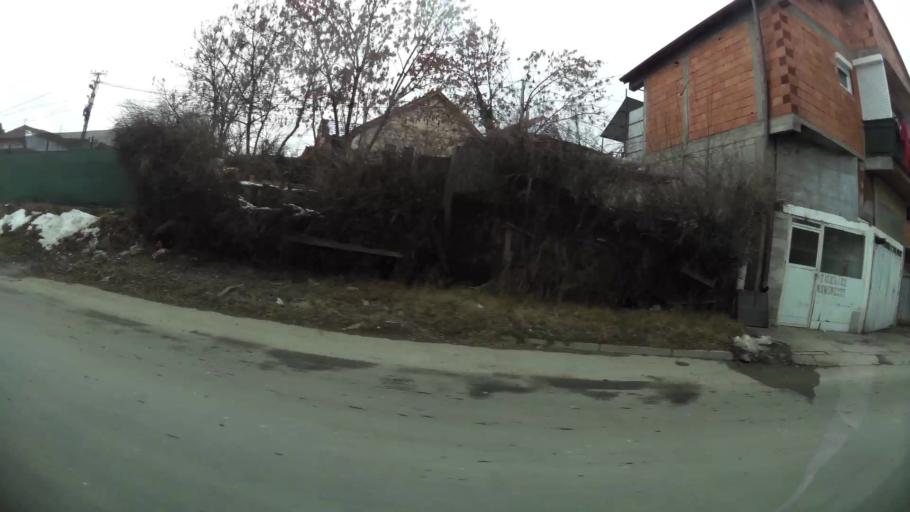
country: MK
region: Butel
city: Butel
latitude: 42.0295
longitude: 21.4345
